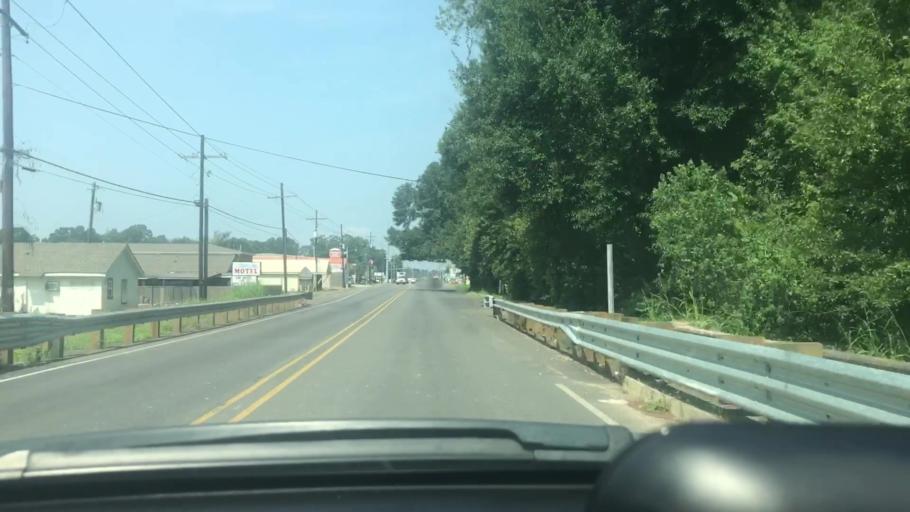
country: US
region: Louisiana
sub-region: Livingston Parish
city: Denham Springs
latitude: 30.4842
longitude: -90.9395
